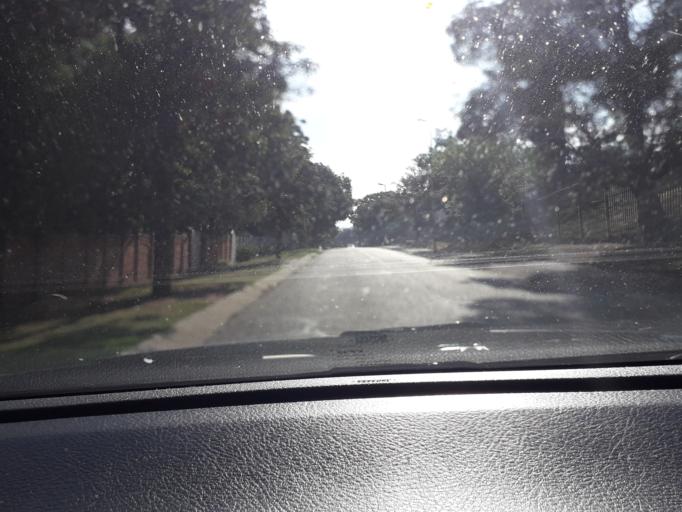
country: ZA
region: Gauteng
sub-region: City of Johannesburg Metropolitan Municipality
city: Modderfontein
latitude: -26.1225
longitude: 28.1296
